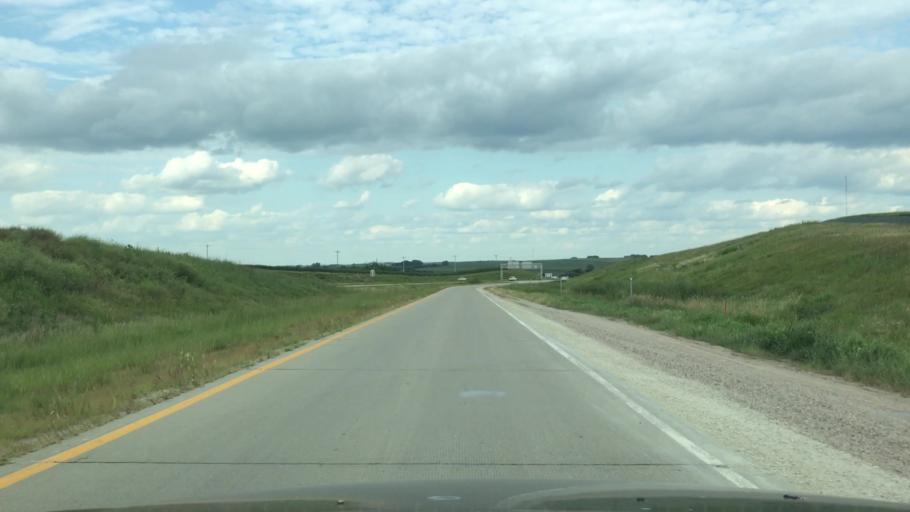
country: US
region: Iowa
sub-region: Plymouth County
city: Le Mars
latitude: 42.8172
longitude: -96.1732
